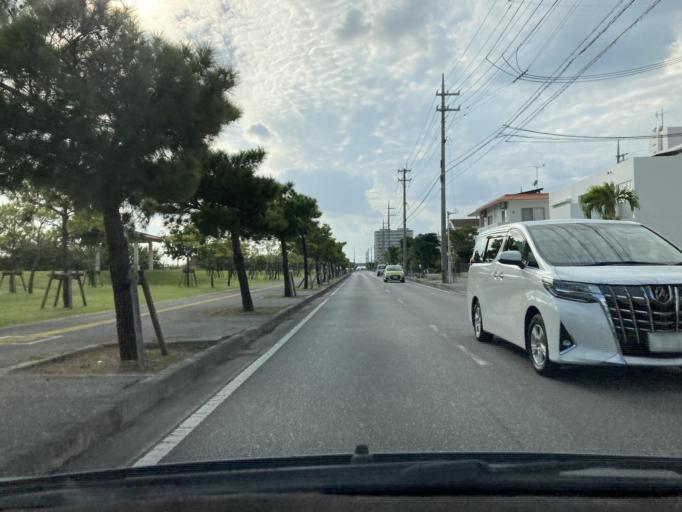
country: JP
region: Okinawa
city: Itoman
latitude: 26.1533
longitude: 127.6653
